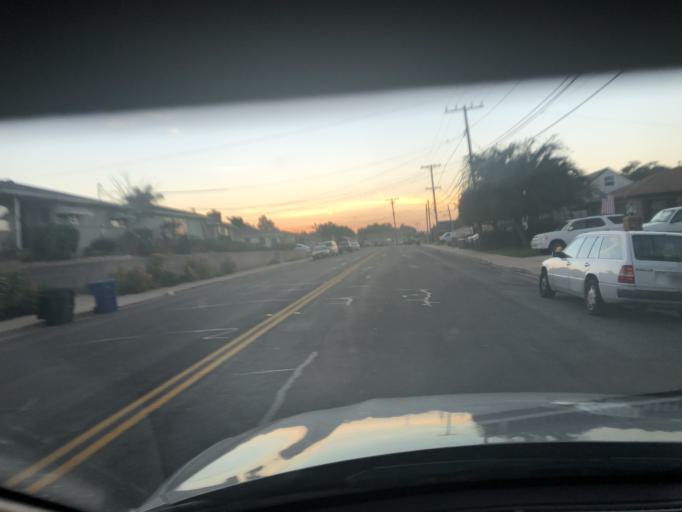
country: US
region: California
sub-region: San Diego County
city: Chula Vista
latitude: 32.6466
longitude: -117.0713
